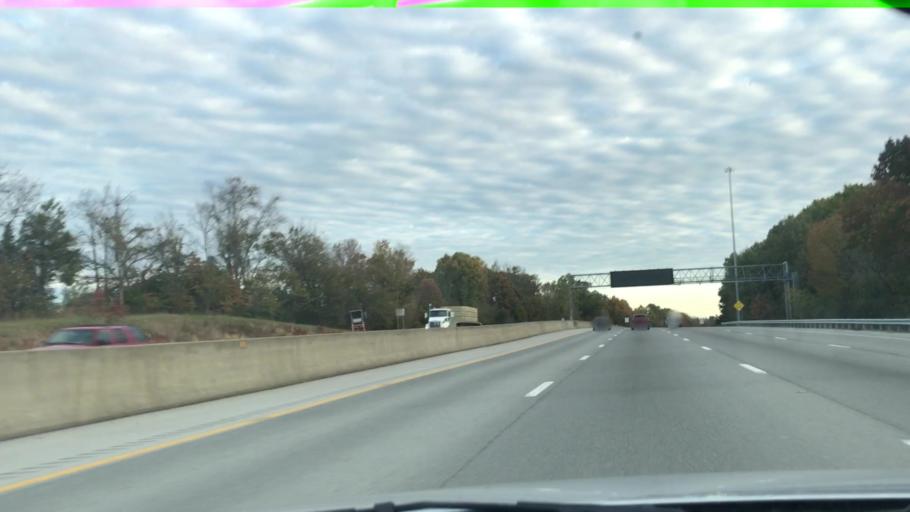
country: US
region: Kentucky
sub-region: Simpson County
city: Franklin
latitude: 36.6473
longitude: -86.5685
